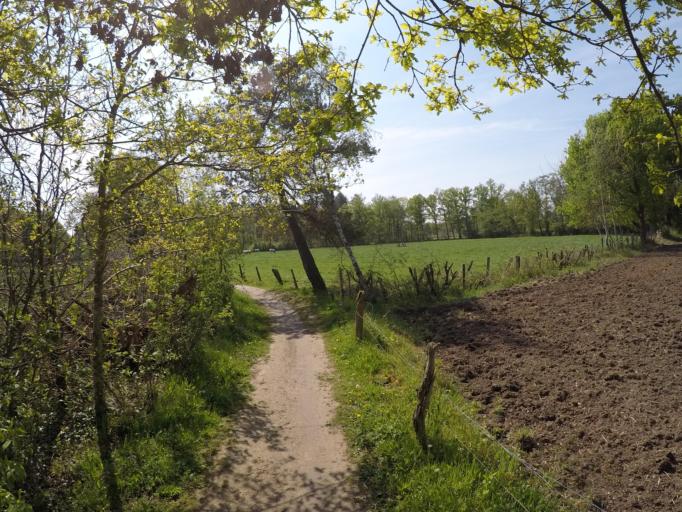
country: BE
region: Flanders
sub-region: Provincie Antwerpen
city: Zandhoven
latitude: 51.2532
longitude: 4.6586
